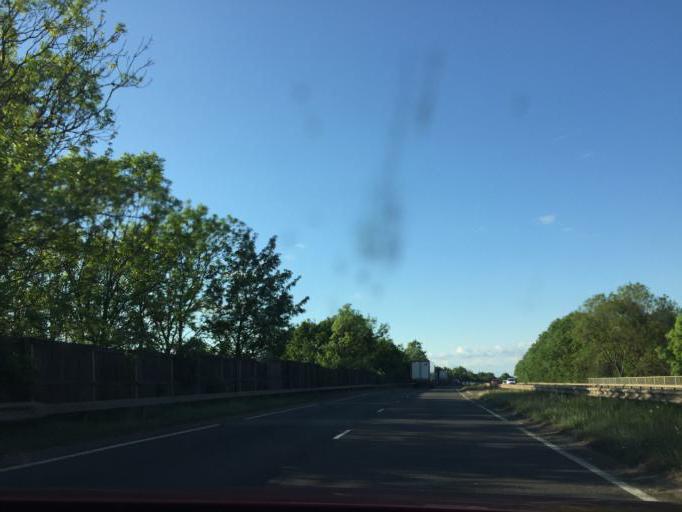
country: GB
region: England
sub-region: Warwickshire
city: Exhall
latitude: 52.4787
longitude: -1.4893
